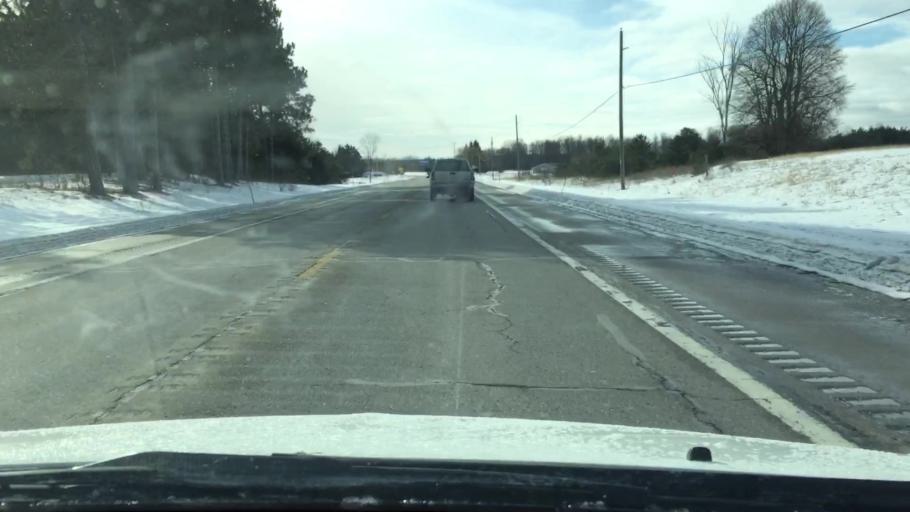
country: US
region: Michigan
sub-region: Wexford County
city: Manton
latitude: 44.5877
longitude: -85.3474
